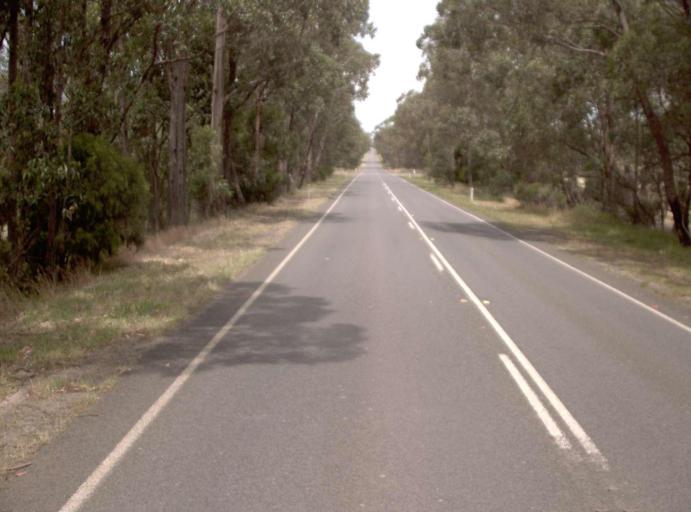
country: AU
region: Victoria
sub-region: Latrobe
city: Traralgon
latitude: -38.5245
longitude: 146.7060
